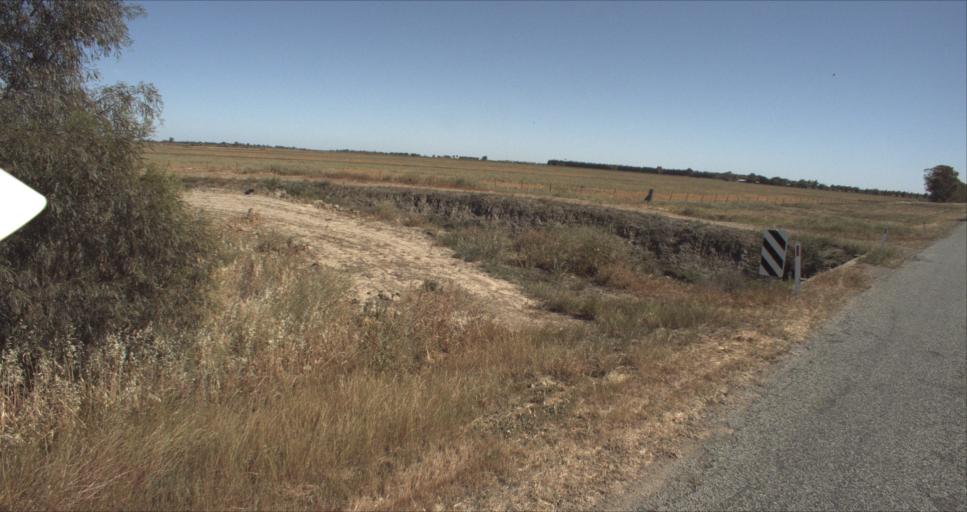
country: AU
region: New South Wales
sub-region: Leeton
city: Leeton
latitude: -34.5398
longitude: 146.3167
